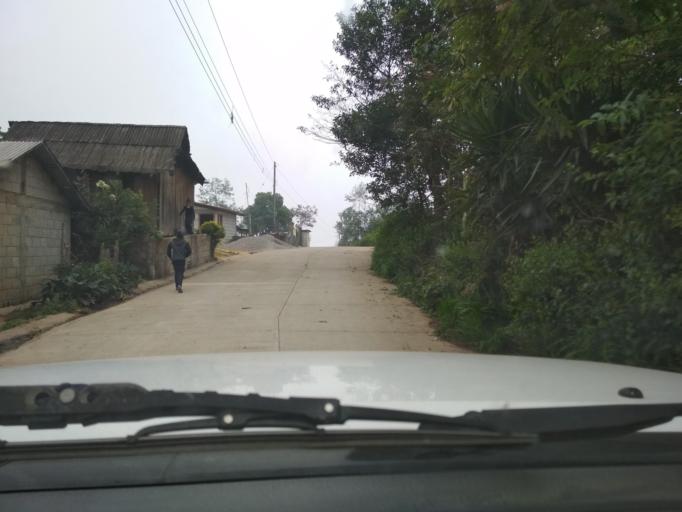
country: MX
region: Veracruz
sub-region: La Perla
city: Chilapa
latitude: 18.9952
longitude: -97.1455
